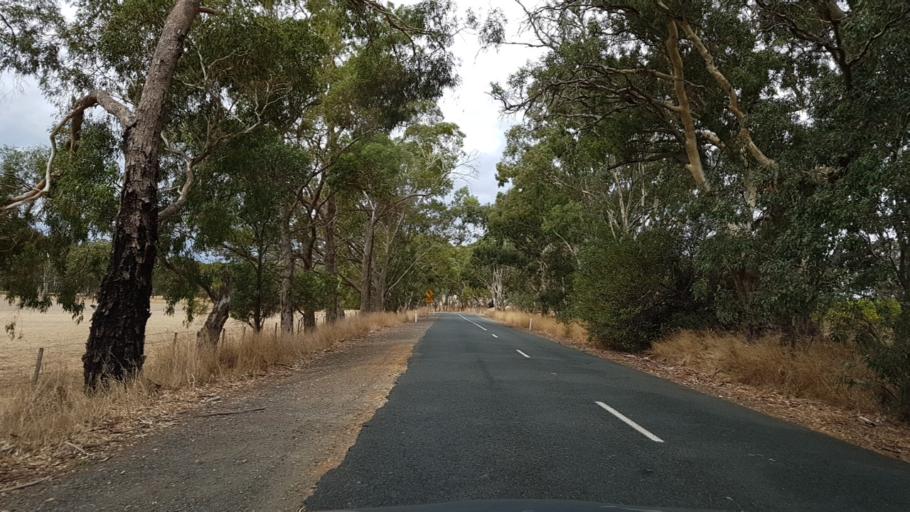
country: AU
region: South Australia
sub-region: Adelaide Hills
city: Birdwood
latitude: -34.7829
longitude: 138.9231
